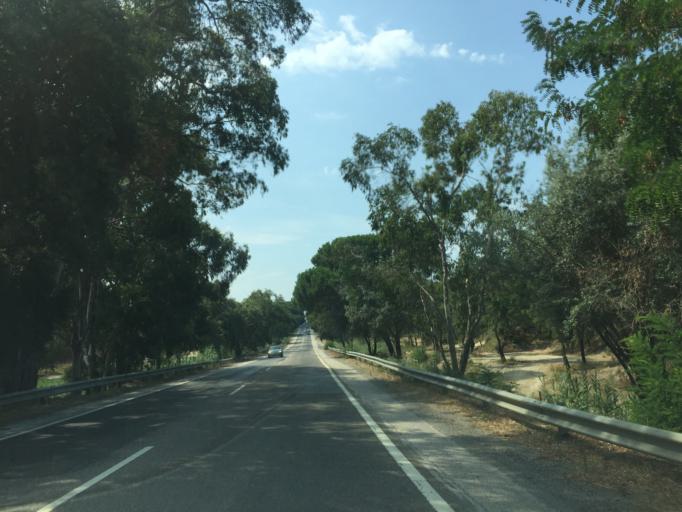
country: PT
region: Setubal
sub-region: Alcacer do Sal
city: Alcacer do Sal
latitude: 38.3409
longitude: -8.5197
